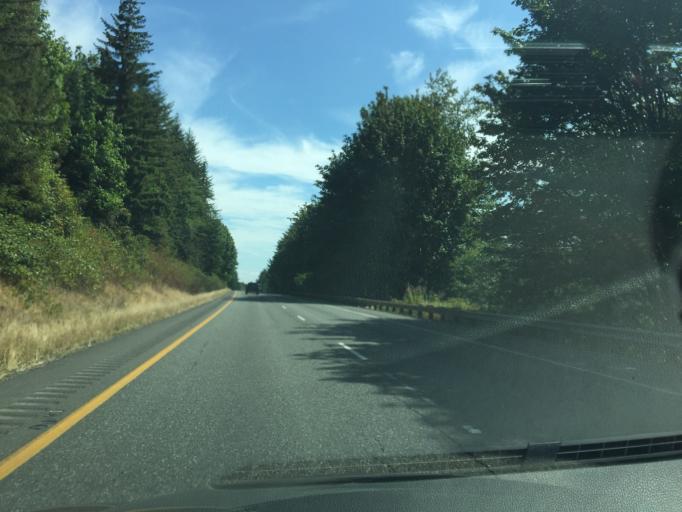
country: US
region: Washington
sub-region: Whatcom County
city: Sudden Valley
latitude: 48.6605
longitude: -122.3712
